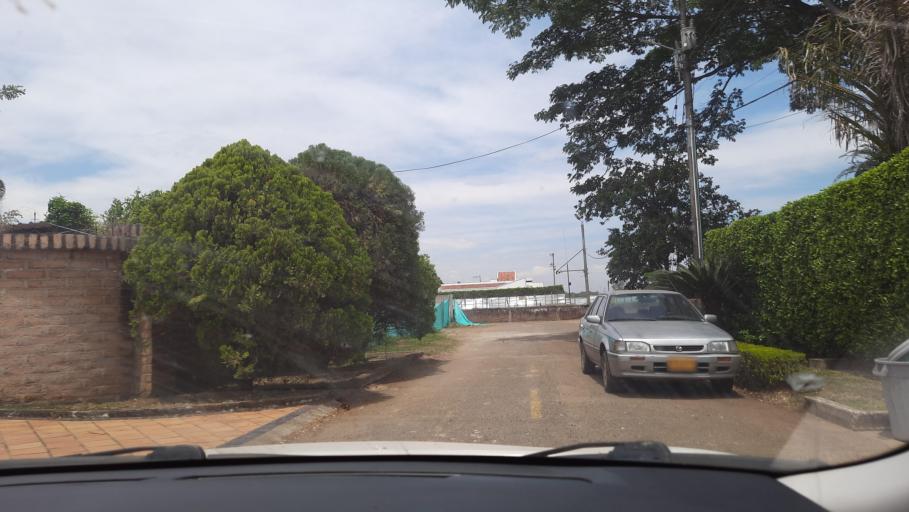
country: CO
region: Valle del Cauca
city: Jamundi
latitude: 3.2677
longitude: -76.5224
